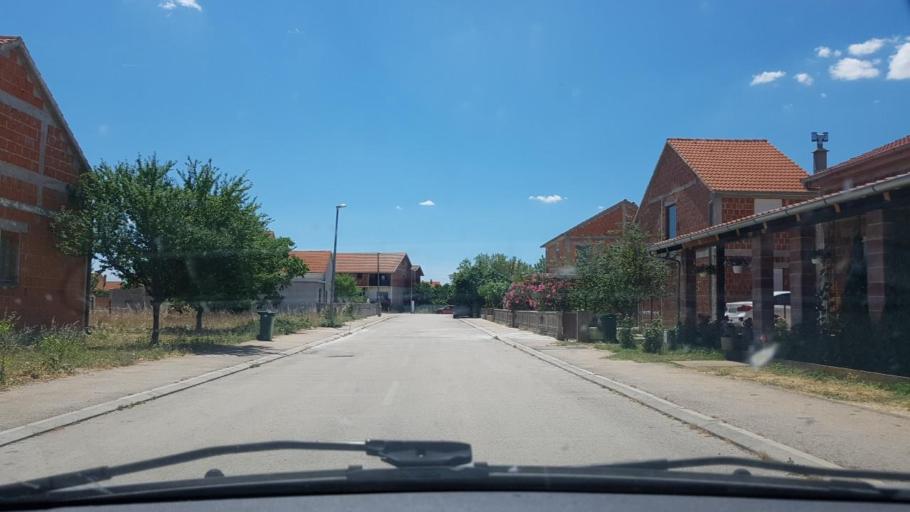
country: HR
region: Sibensko-Kniniska
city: Kistanje
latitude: 43.9823
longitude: 15.9726
